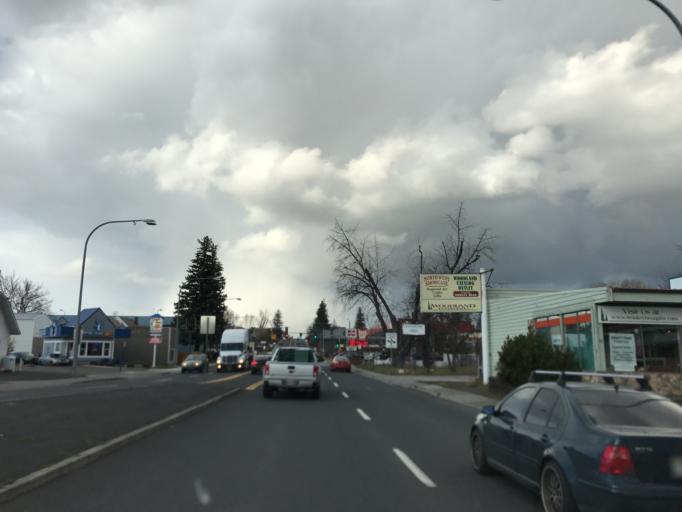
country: US
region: Idaho
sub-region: Latah County
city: Moscow
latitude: 46.7362
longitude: -117.0014
